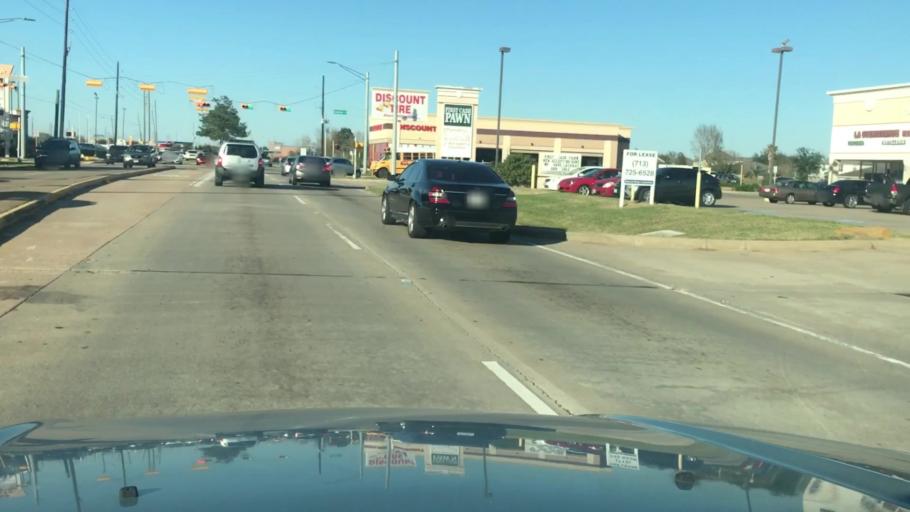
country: US
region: Texas
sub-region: Harris County
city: Cypress
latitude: 29.8543
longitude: -95.7186
